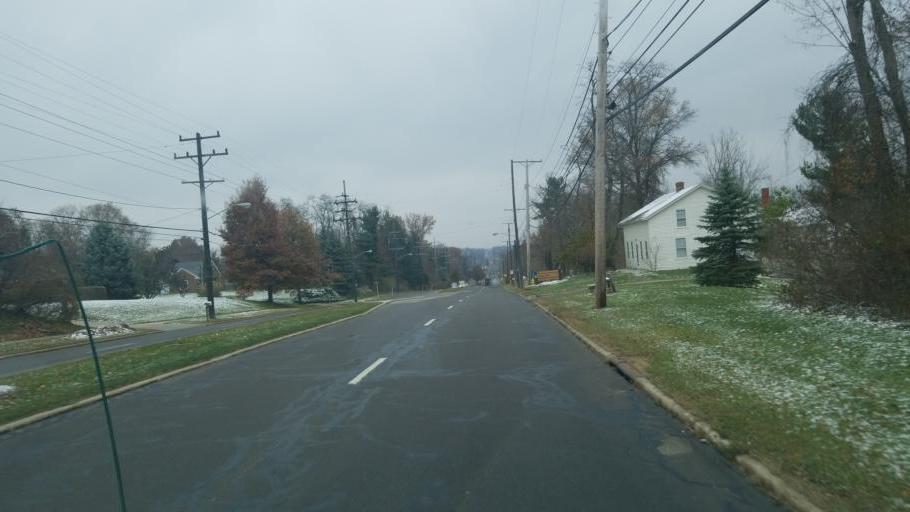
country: US
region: Ohio
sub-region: Cuyahoga County
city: Brecksville
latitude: 41.3066
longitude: -81.6268
